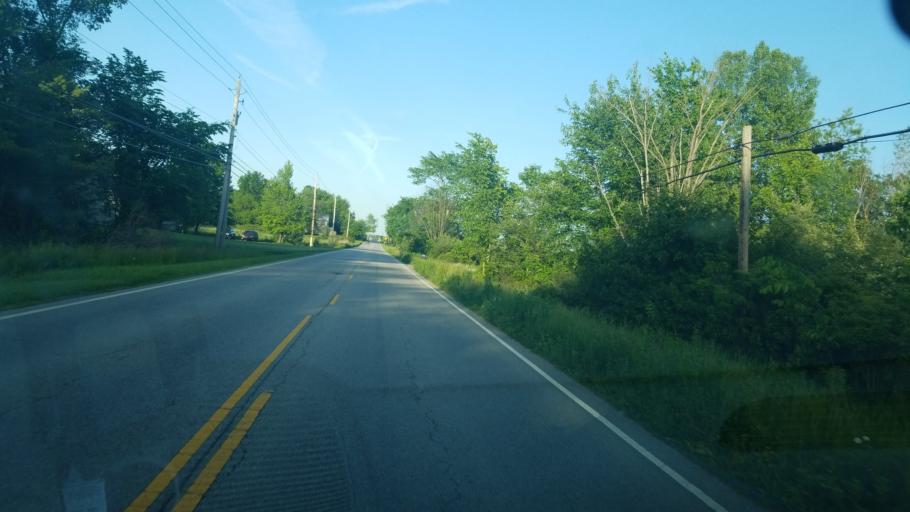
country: US
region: Ohio
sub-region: Trumbull County
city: Lordstown
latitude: 41.0993
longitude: -80.8989
